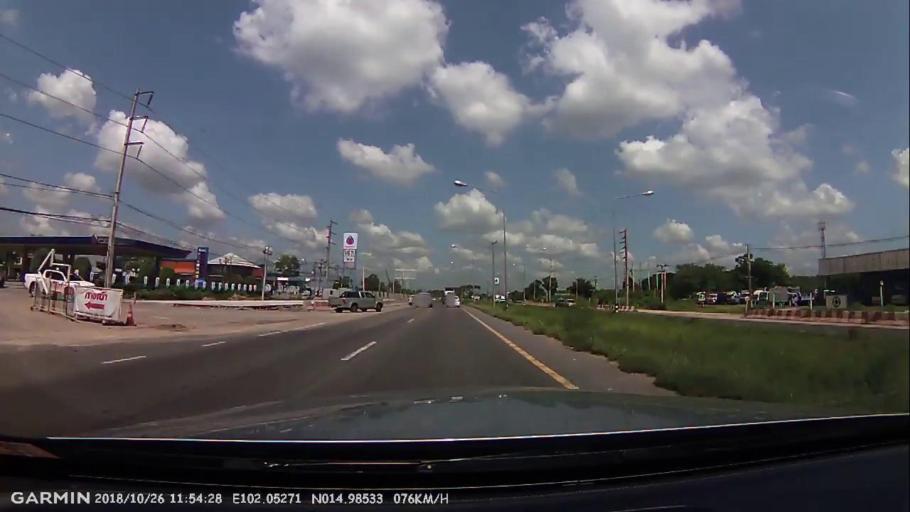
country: TH
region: Nakhon Ratchasima
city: Nakhon Ratchasima
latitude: 14.9855
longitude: 102.0527
